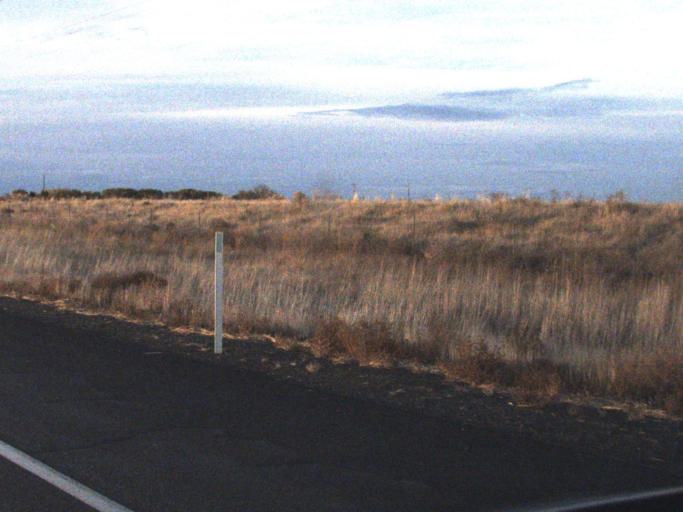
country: US
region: Washington
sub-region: Walla Walla County
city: Burbank
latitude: 46.1852
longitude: -118.9781
